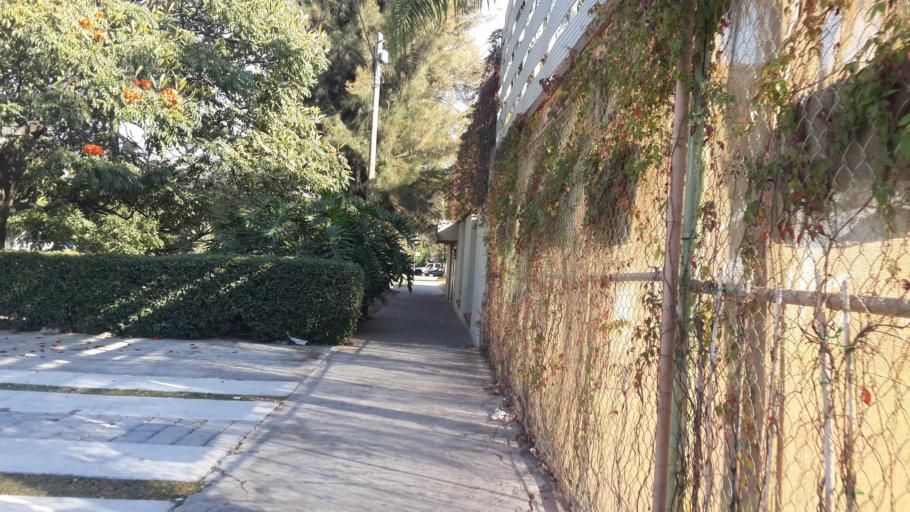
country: MX
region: Jalisco
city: Guadalajara
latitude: 20.6697
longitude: -103.4321
